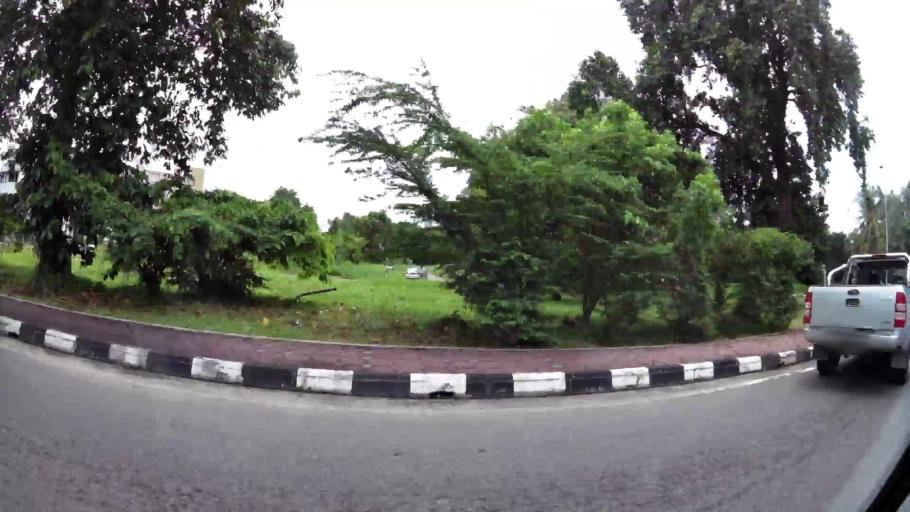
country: BN
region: Brunei and Muara
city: Bandar Seri Begawan
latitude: 4.9100
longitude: 114.9196
